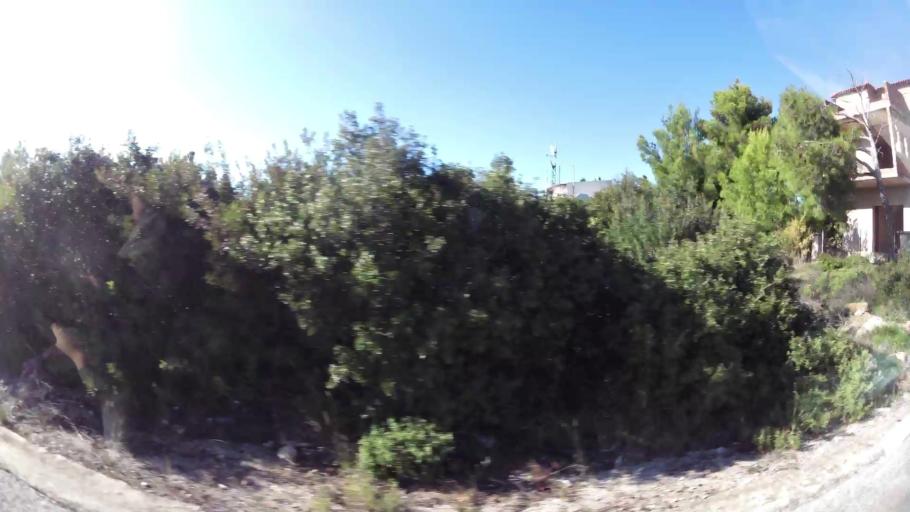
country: GR
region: Attica
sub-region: Nomarchia Anatolikis Attikis
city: Anthousa
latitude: 38.0319
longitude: 23.8726
